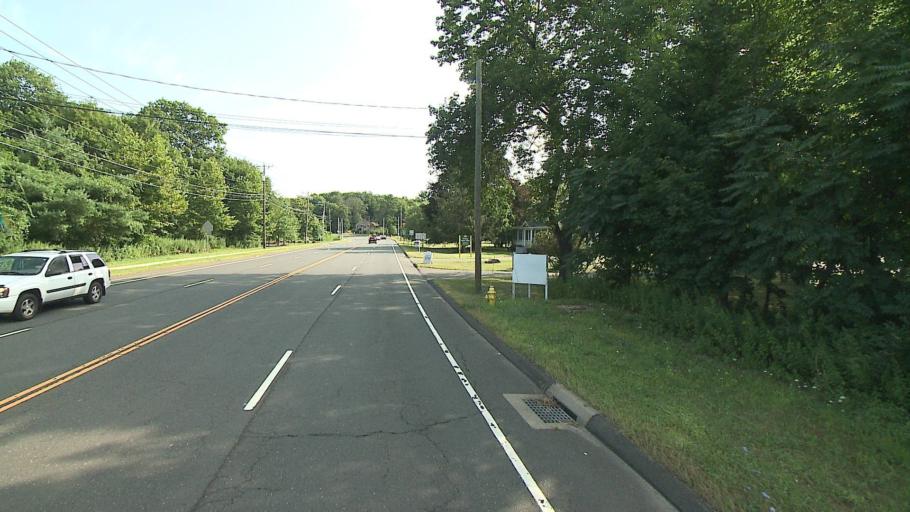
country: US
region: Connecticut
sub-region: Fairfield County
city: Wilton
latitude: 41.2155
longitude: -73.4301
